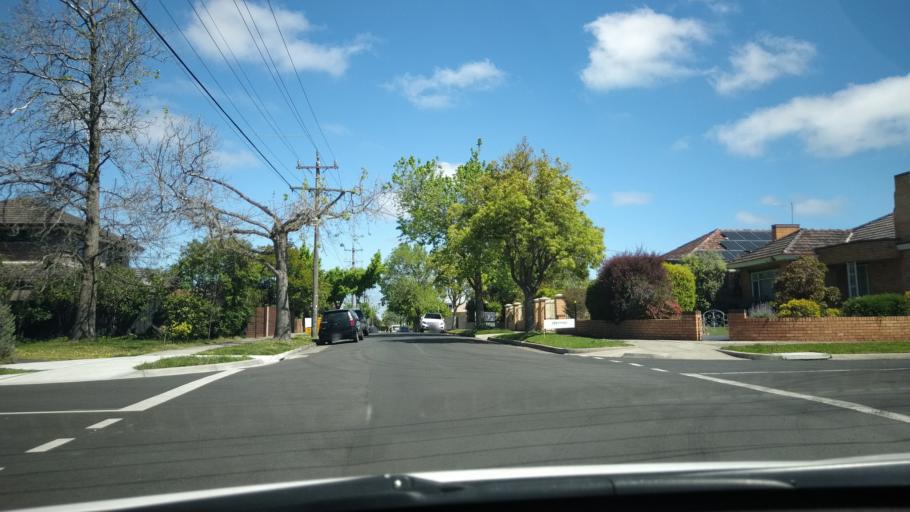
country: AU
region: Victoria
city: Murrumbeena
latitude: -37.9050
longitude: 145.0691
